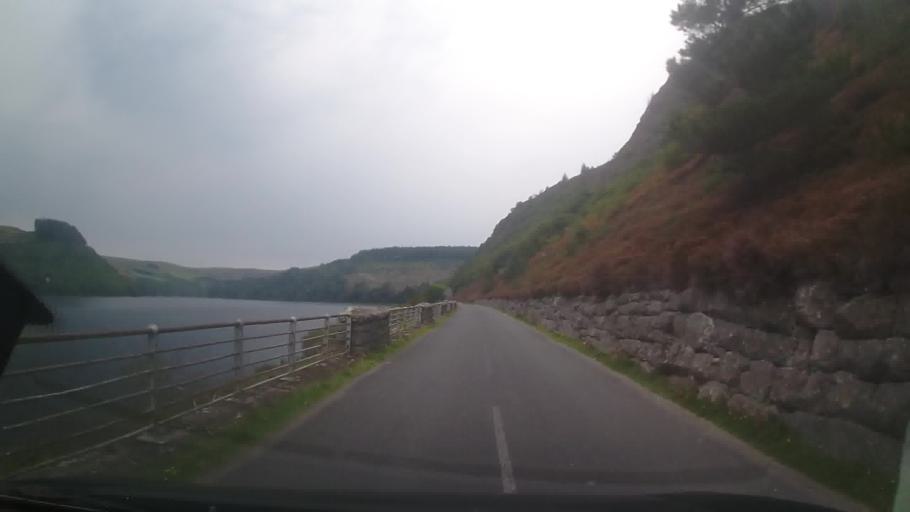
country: GB
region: Wales
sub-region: Sir Powys
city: Rhayader
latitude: 52.2669
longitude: -3.5830
